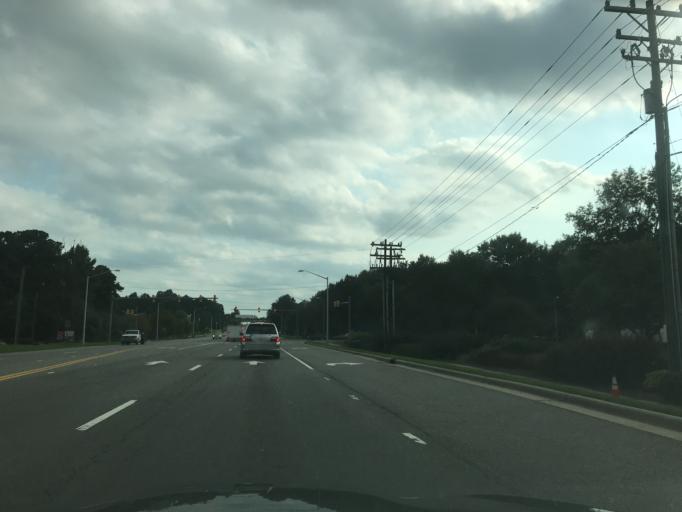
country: US
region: North Carolina
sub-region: Durham County
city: Durham
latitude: 35.9117
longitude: -78.8927
